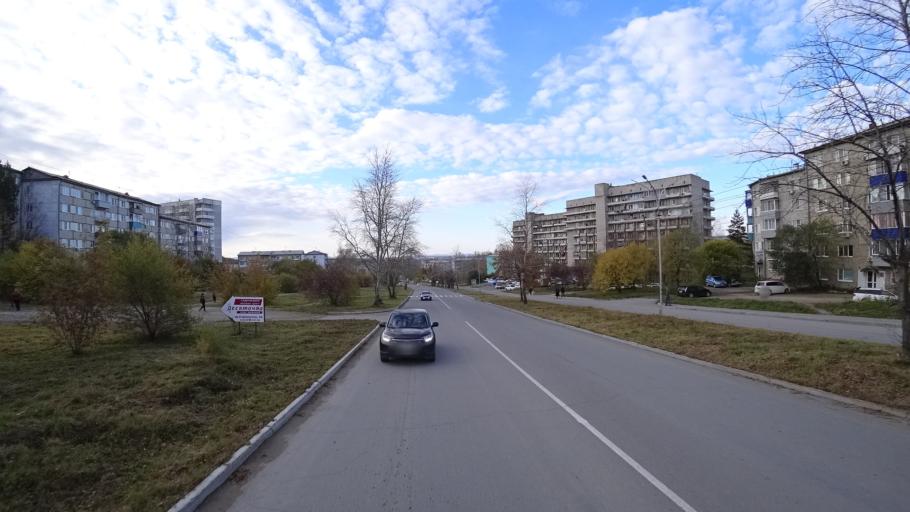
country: RU
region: Khabarovsk Krai
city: Amursk
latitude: 50.2405
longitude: 136.9126
